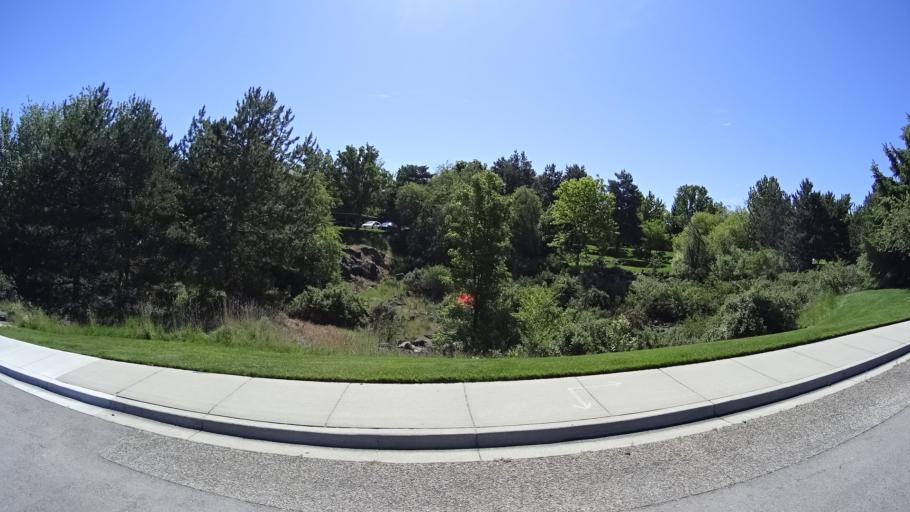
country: US
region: Idaho
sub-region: Ada County
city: Boise
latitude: 43.5444
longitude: -116.1549
